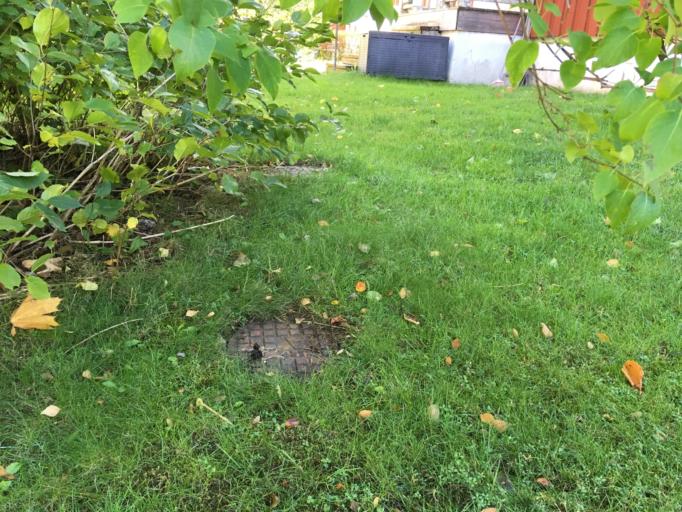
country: SE
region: Vaermland
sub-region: Hammaro Kommun
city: Skoghall
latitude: 59.3243
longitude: 13.4631
